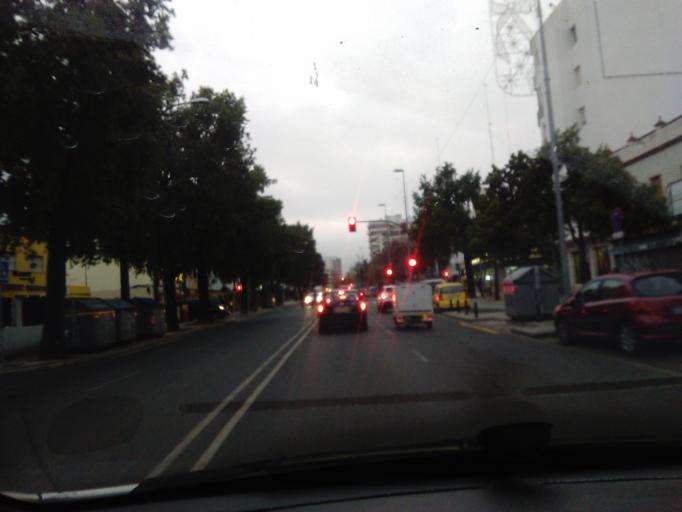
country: ES
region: Andalusia
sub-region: Provincia de Sevilla
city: Sevilla
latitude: 37.3811
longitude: -5.9614
